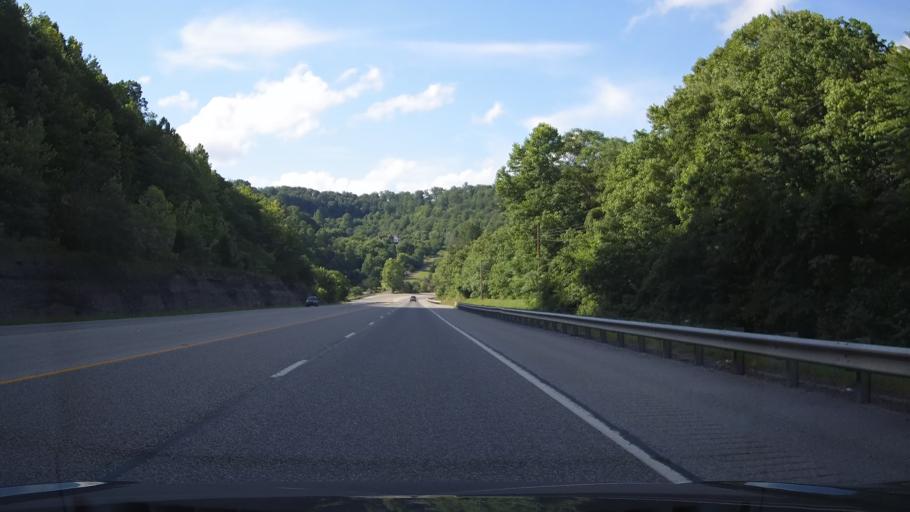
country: US
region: Kentucky
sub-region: Lawrence County
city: Louisa
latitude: 38.0048
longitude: -82.6643
